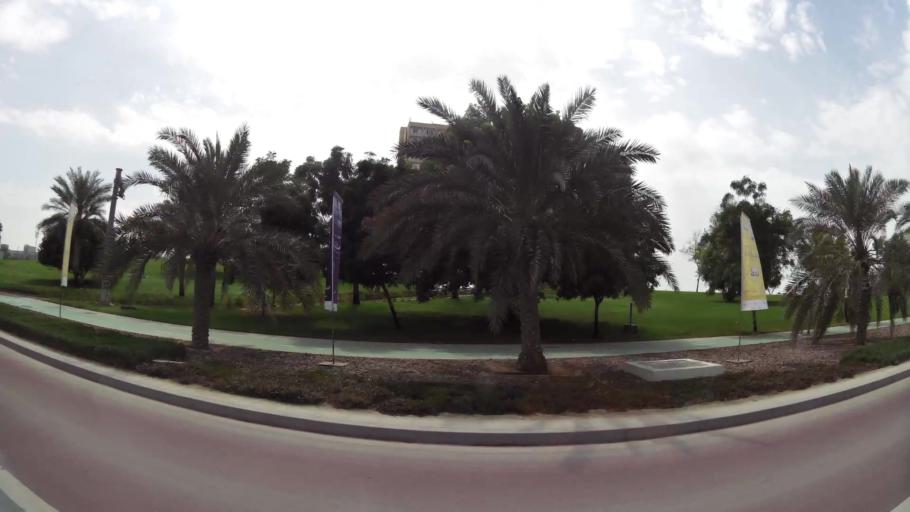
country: AE
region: Abu Dhabi
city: Abu Dhabi
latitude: 24.4590
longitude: 54.3293
